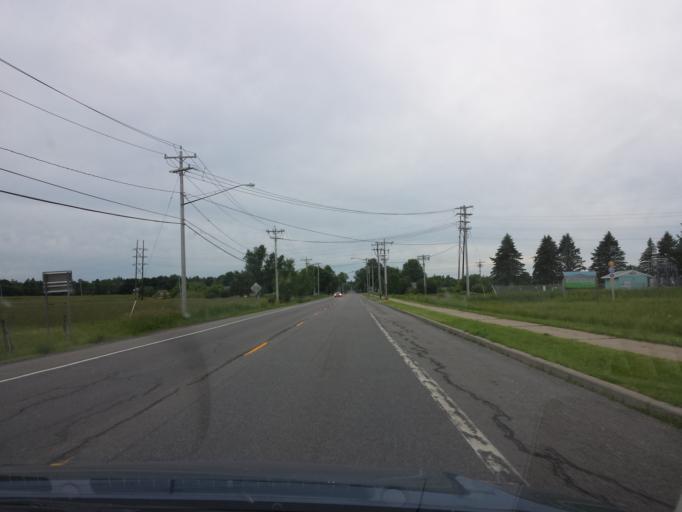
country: US
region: New York
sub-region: St. Lawrence County
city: Potsdam
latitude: 44.6790
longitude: -74.9692
